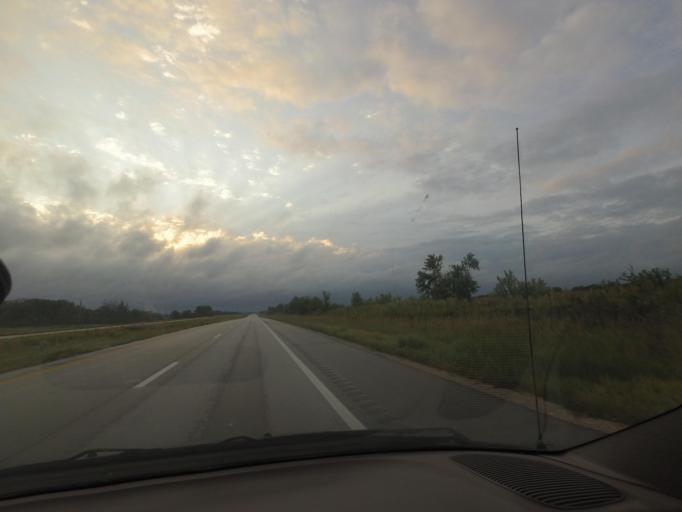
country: US
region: Missouri
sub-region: Shelby County
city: Shelbina
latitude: 39.6819
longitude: -91.9894
